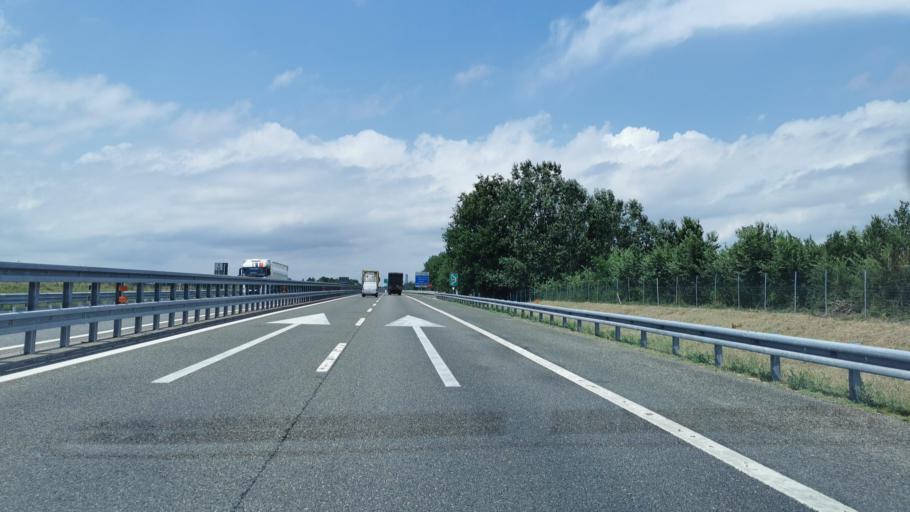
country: IT
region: Piedmont
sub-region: Provincia di Alessandria
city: Quattordio
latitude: 44.9118
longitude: 8.4182
